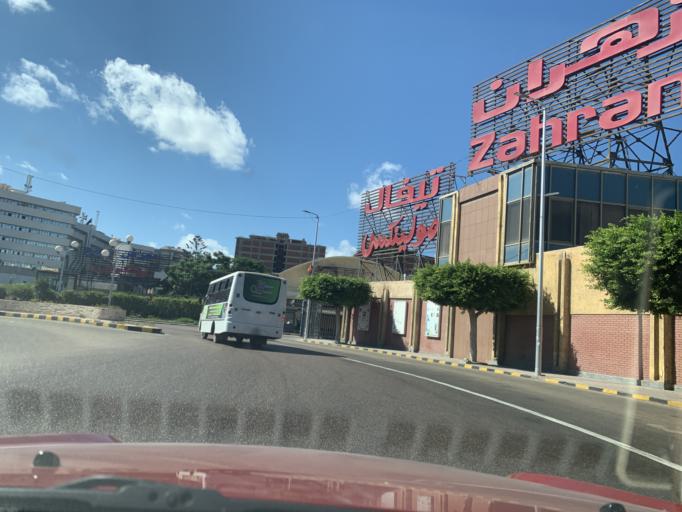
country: EG
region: Alexandria
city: Alexandria
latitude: 31.2121
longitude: 29.9555
